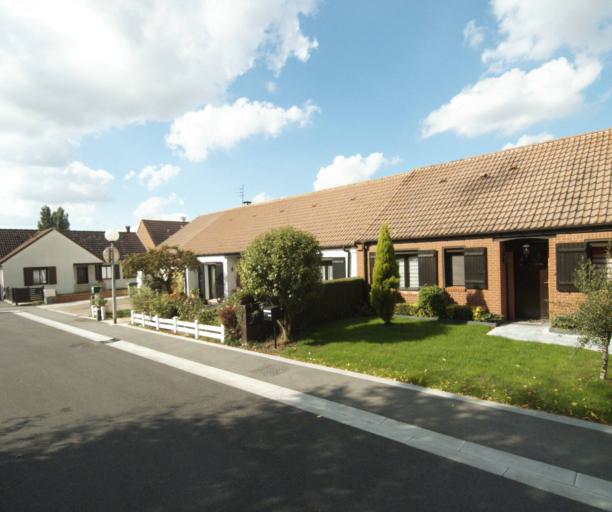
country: FR
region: Nord-Pas-de-Calais
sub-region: Departement du Nord
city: Herlies
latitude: 50.5737
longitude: 2.8697
